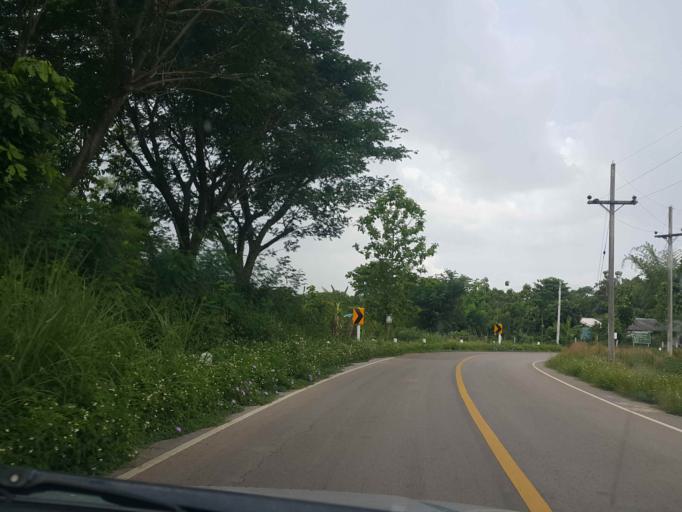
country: TH
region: Phayao
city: Dok Kham Tai
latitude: 19.0408
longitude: 99.9550
